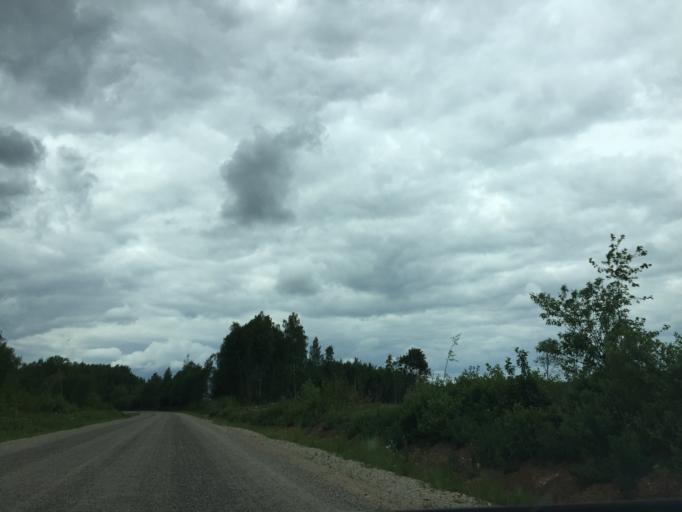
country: LV
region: Dagda
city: Dagda
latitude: 56.0669
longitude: 27.5601
